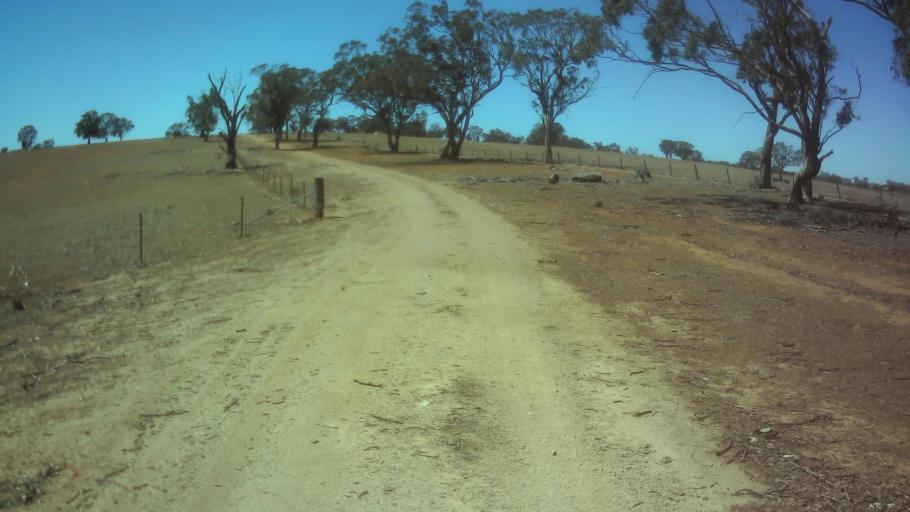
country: AU
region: New South Wales
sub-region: Cowra
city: Cowra
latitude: -33.8983
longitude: 148.5066
